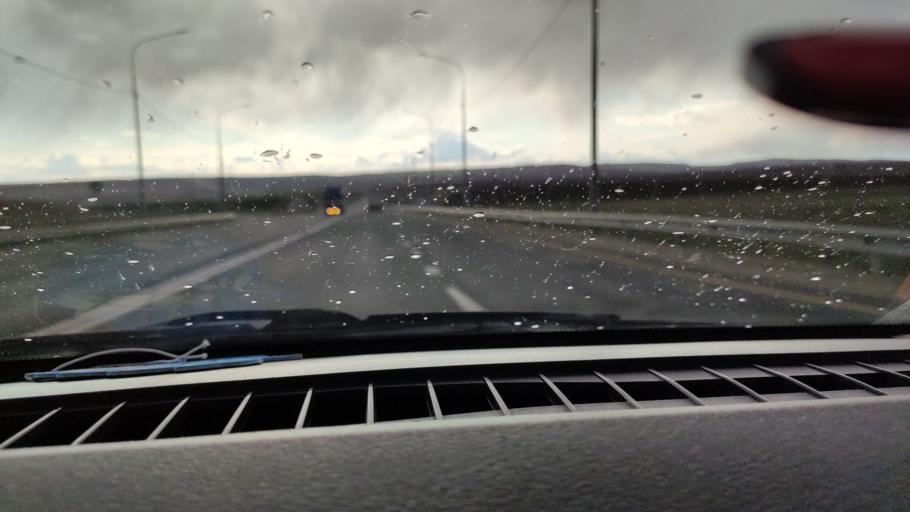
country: RU
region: Saratov
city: Yelshanka
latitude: 51.8303
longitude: 46.4186
